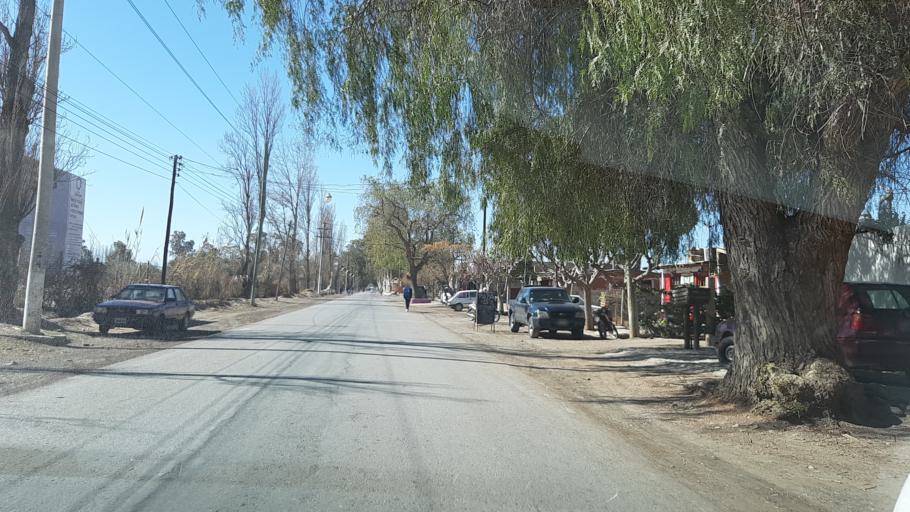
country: AR
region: San Juan
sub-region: Departamento de Zonda
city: Zonda
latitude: -31.4695
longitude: -68.7444
